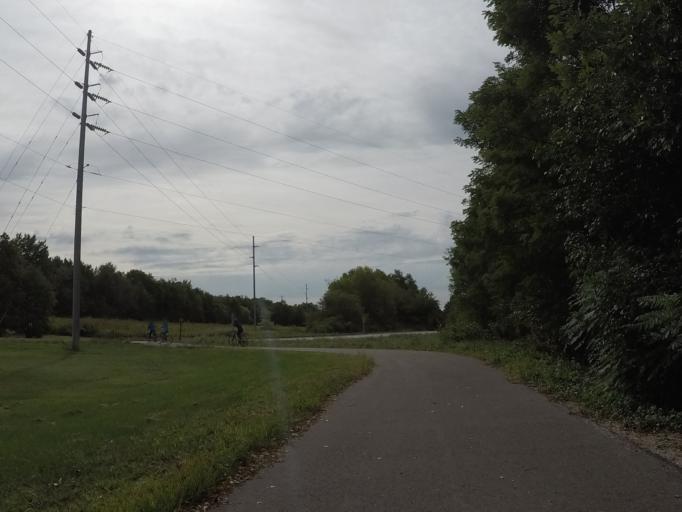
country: US
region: Wisconsin
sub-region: Sauk County
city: Prairie du Sac
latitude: 43.3146
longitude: -89.7356
